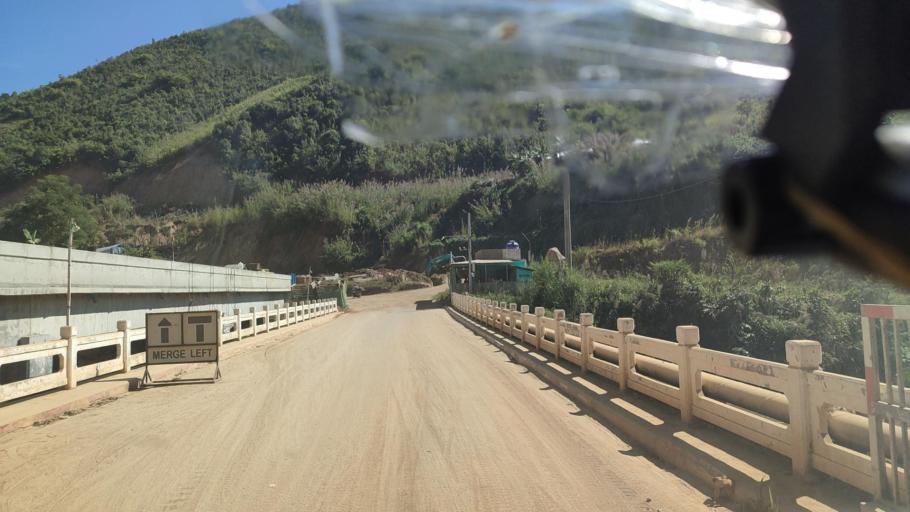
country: TH
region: Chiang Rai
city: Mae Sai
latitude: 21.2772
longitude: 99.5582
